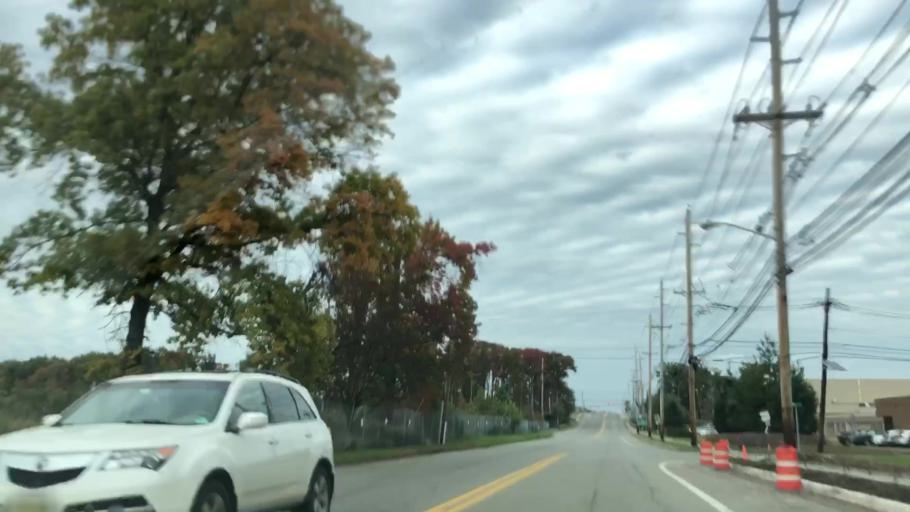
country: US
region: New Jersey
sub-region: Passaic County
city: Singac
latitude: 40.8892
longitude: -74.2289
